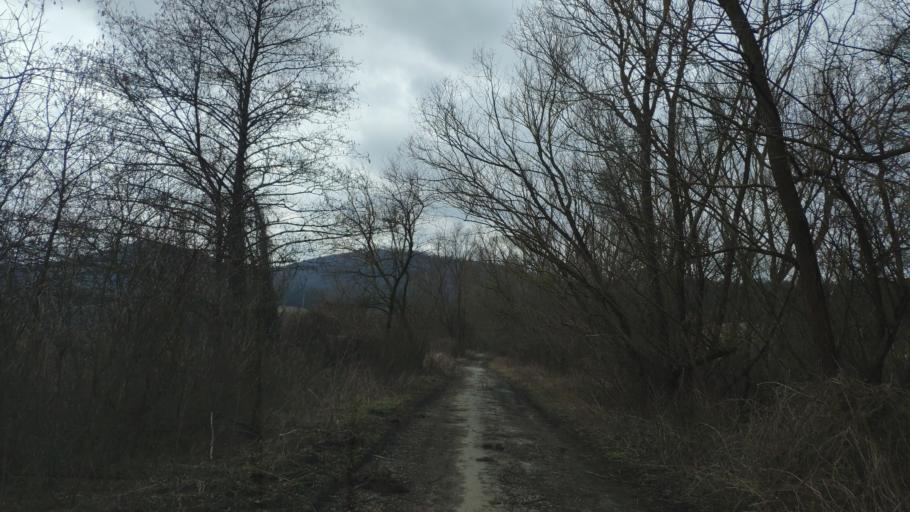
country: SK
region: Presovsky
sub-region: Okres Presov
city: Presov
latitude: 49.0807
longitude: 21.2867
